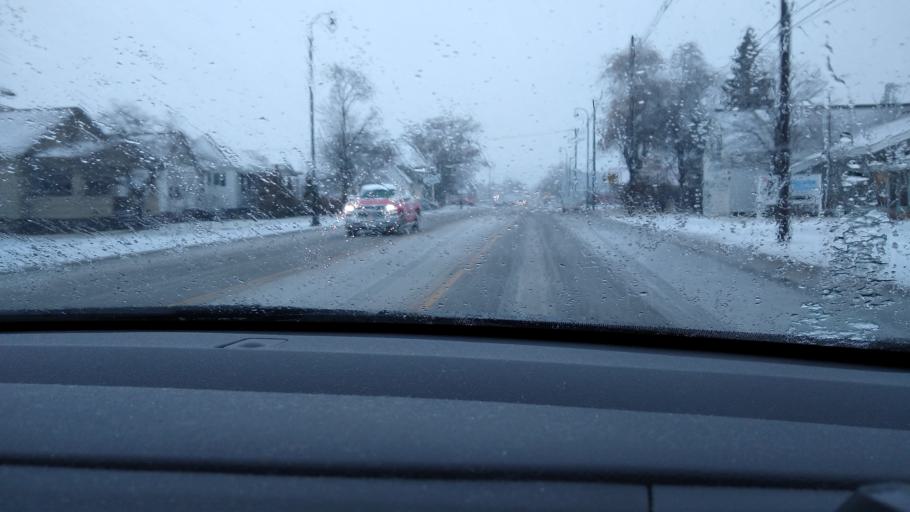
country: US
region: Michigan
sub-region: Delta County
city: Escanaba
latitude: 45.7525
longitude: -87.0718
